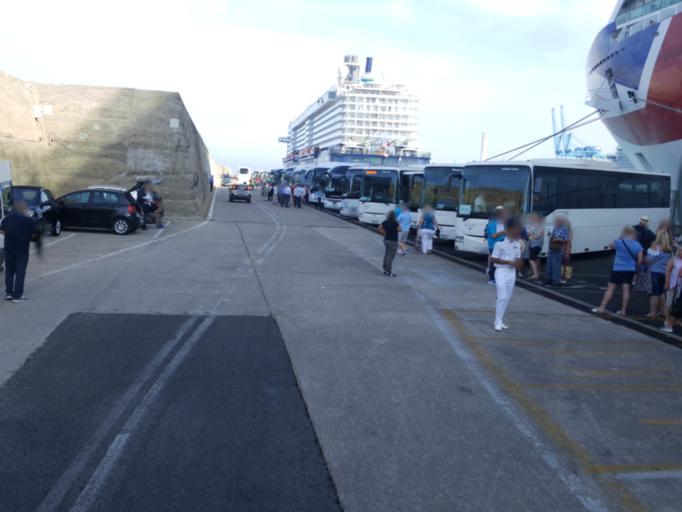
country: IT
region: Latium
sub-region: Citta metropolitana di Roma Capitale
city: Civitavecchia
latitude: 42.0982
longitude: 11.7745
